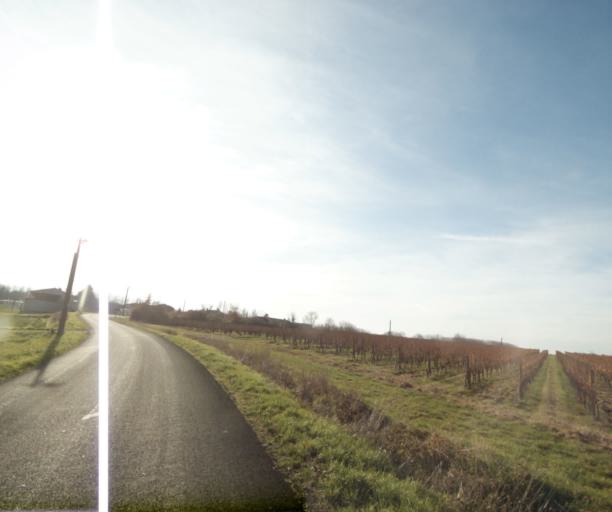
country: FR
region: Poitou-Charentes
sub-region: Departement de la Charente-Maritime
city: Chaniers
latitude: 45.7119
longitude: -0.5259
